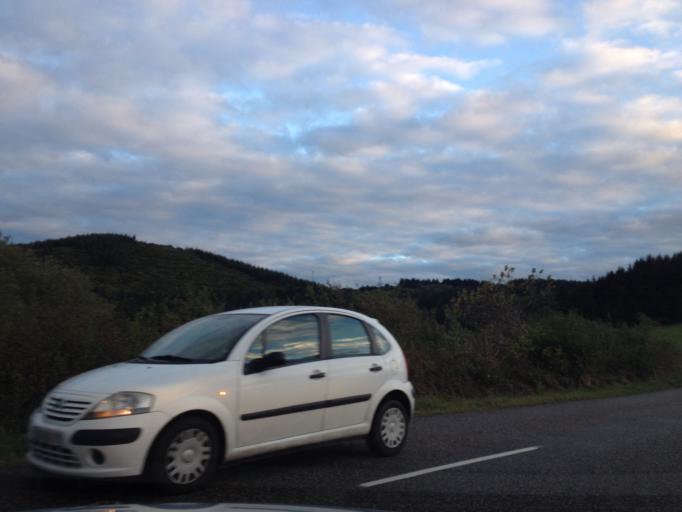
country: FR
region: Rhone-Alpes
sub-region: Departement de la Loire
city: Renaison
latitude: 46.0038
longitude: 3.8868
